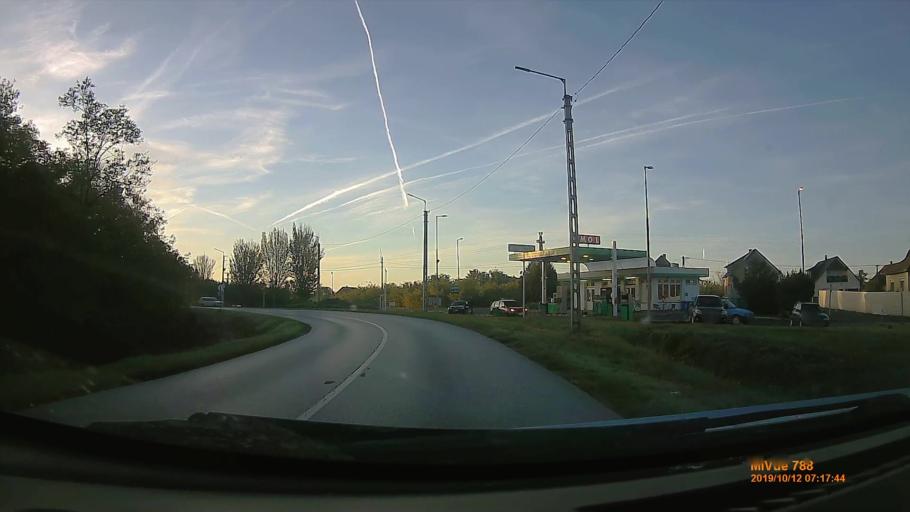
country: HU
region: Hajdu-Bihar
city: Hosszupalyi
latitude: 47.4010
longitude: 21.7229
